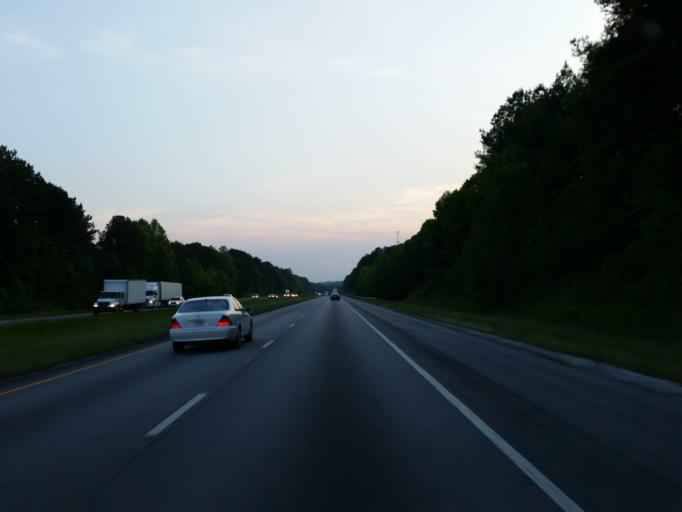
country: US
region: Alabama
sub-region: Cleburne County
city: Heflin
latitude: 33.6268
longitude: -85.5633
